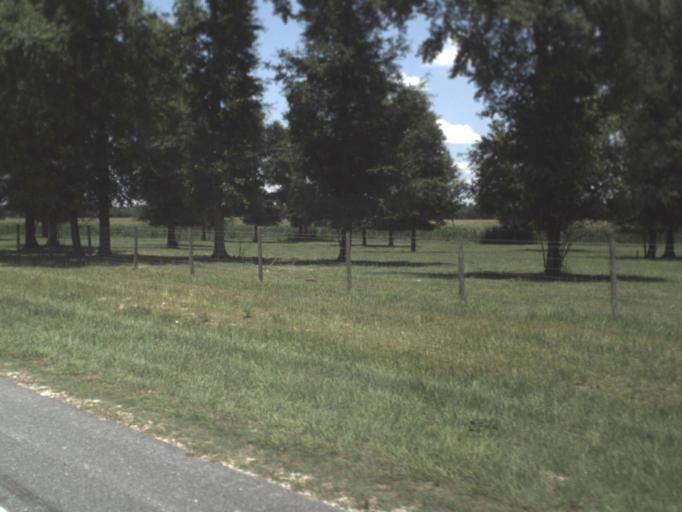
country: US
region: Florida
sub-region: Dixie County
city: Cross City
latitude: 29.8258
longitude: -82.9685
